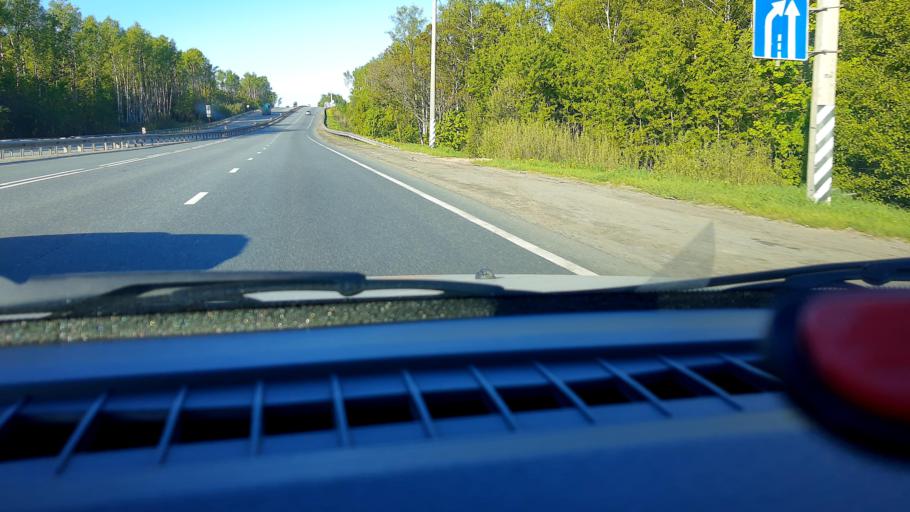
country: RU
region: Vladimir
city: Gorokhovets
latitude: 56.1824
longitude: 42.6670
